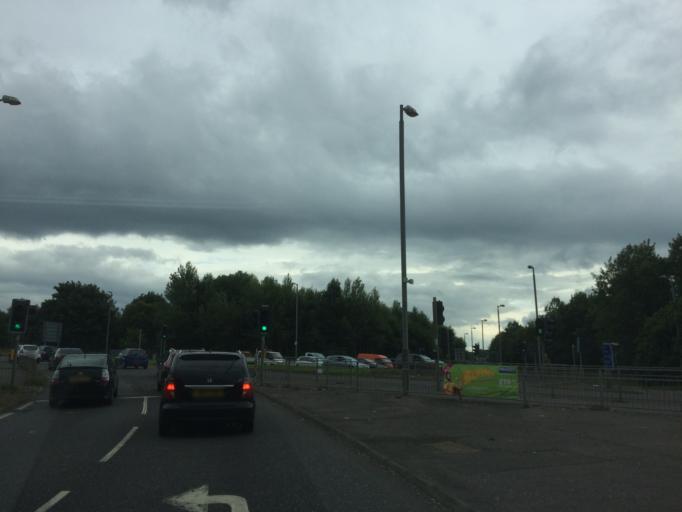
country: GB
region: Scotland
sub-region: East Renfrewshire
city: Newton Mearns
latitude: 55.8045
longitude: -4.3359
